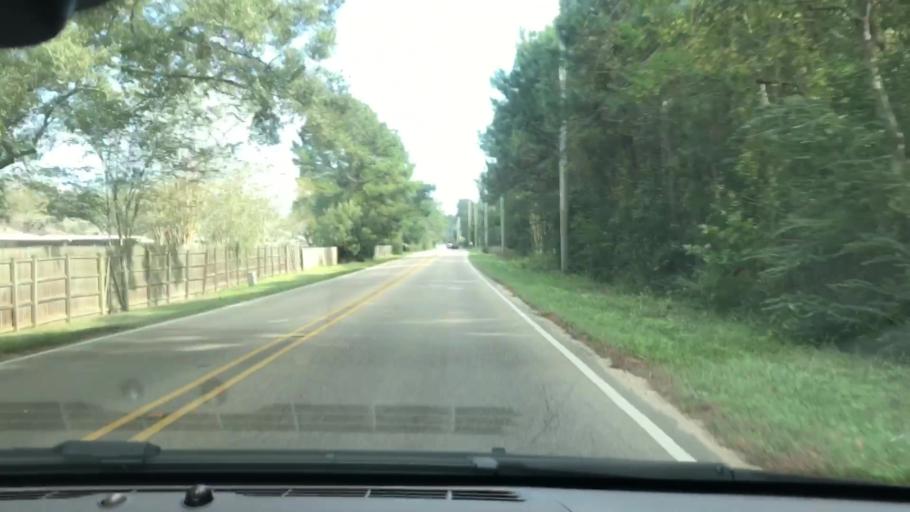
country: US
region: Louisiana
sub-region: Saint Tammany Parish
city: Abita Springs
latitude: 30.4599
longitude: -90.0491
